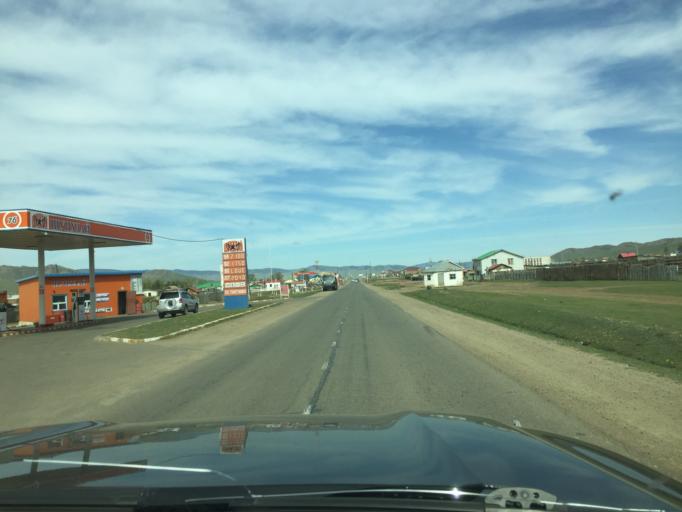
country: MN
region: Central Aimak
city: Ihsueuej
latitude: 48.2204
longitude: 106.3001
